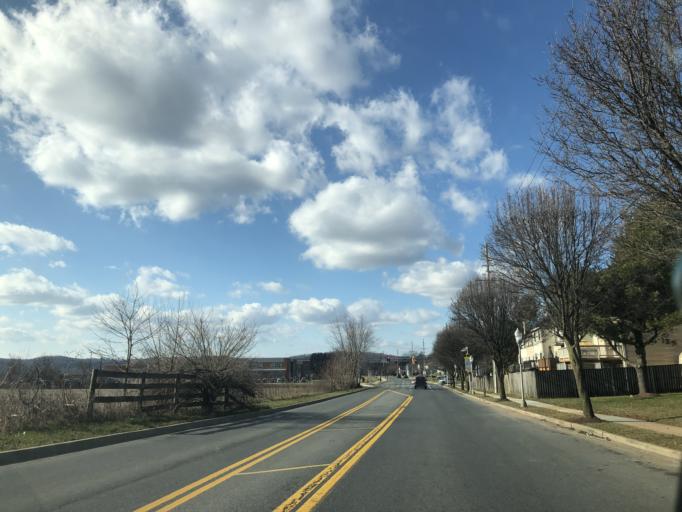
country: US
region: Maryland
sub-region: Frederick County
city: Ballenger Creek
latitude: 39.4088
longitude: -77.4520
